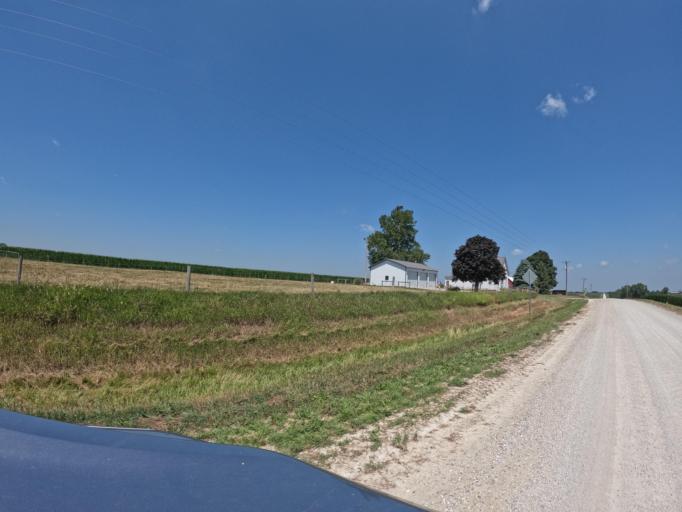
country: US
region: Iowa
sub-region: Keokuk County
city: Sigourney
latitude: 41.2669
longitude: -92.2382
